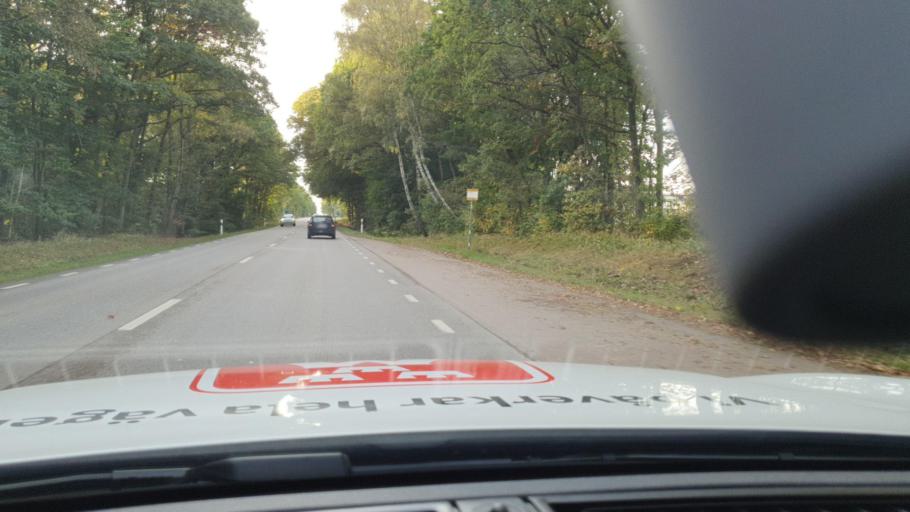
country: SE
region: Skane
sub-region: Angelholms Kommun
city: Munka-Ljungby
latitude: 56.2539
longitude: 12.9926
